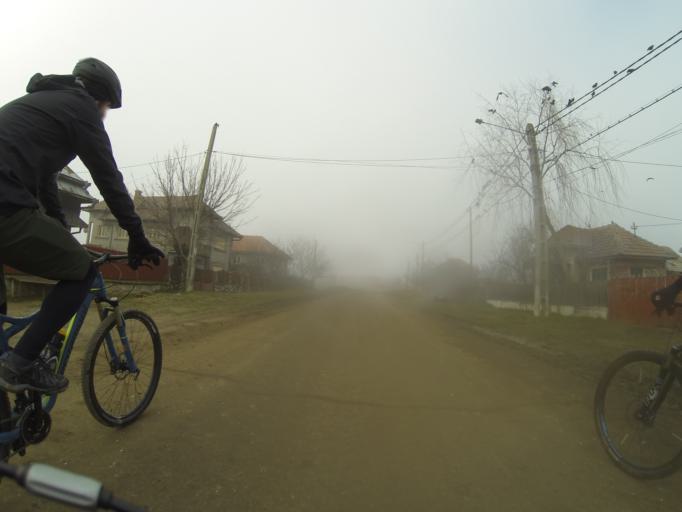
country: RO
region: Mehedinti
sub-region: Comuna Baclesu
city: Baclesu
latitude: 44.4783
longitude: 23.1101
